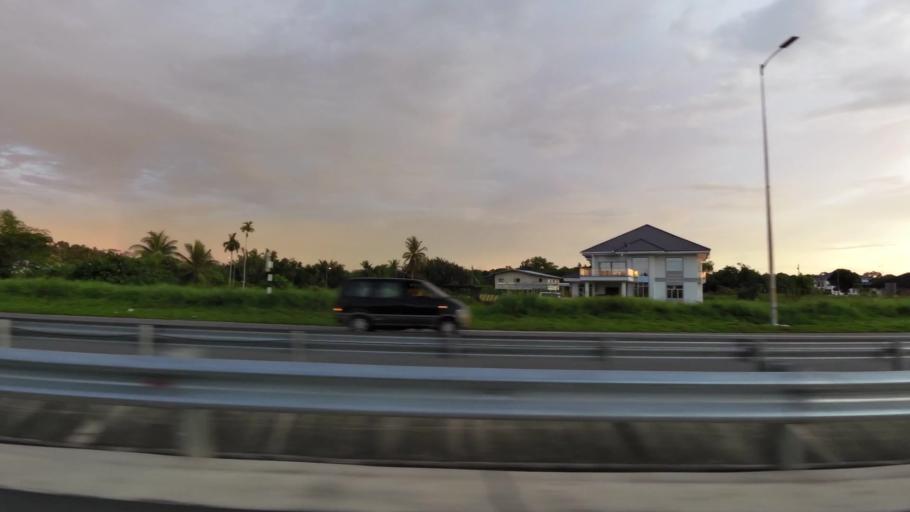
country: BN
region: Belait
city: Kuala Belait
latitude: 4.5803
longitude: 114.2463
